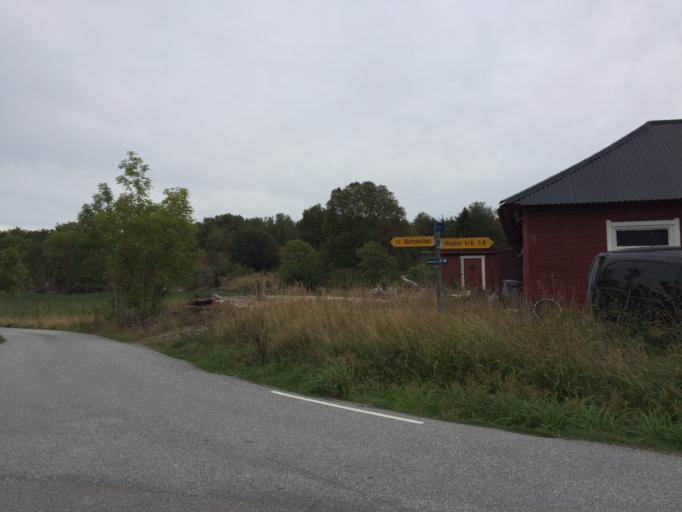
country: NO
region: Ostfold
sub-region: Hvaler
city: Skjaerhalden
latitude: 59.0629
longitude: 11.0337
